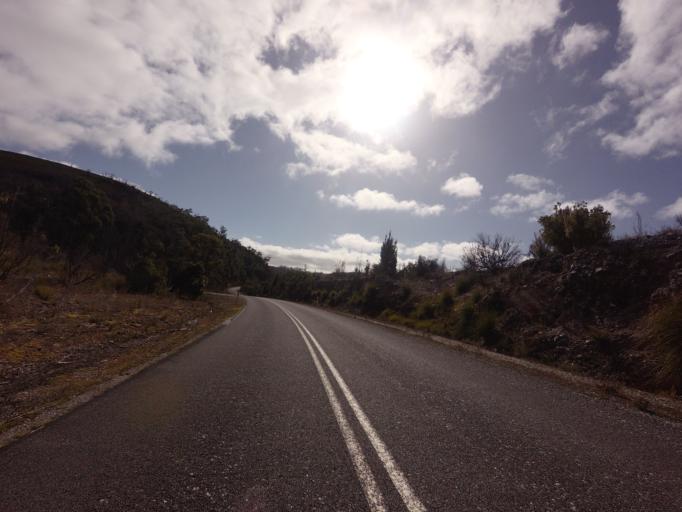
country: AU
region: Tasmania
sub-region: Huon Valley
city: Geeveston
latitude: -42.8600
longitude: 146.2285
